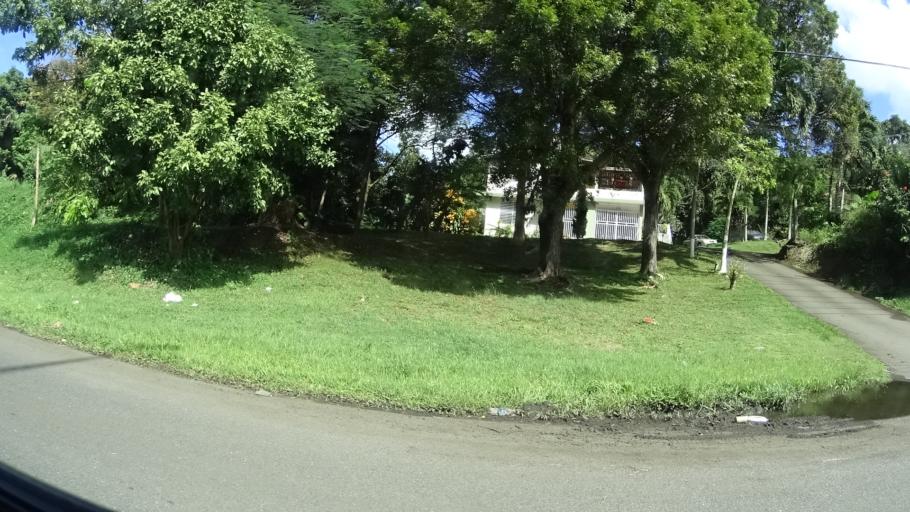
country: PR
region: Rio Grande
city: Hato Candal
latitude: 18.3726
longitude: -65.7827
